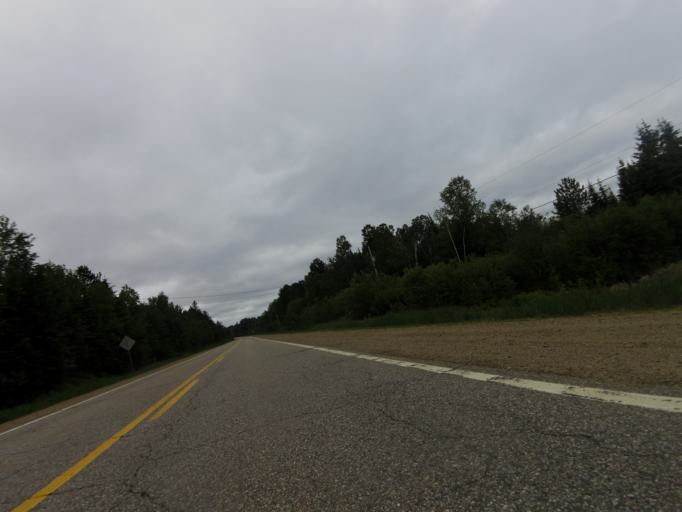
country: CA
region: Quebec
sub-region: Outaouais
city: Shawville
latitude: 45.8760
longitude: -76.4011
